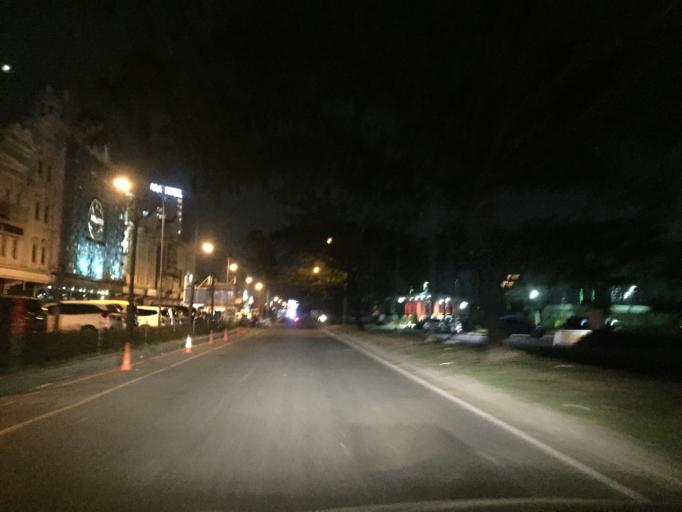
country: ID
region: Banten
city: Tangerang
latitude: -6.2433
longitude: 106.6282
